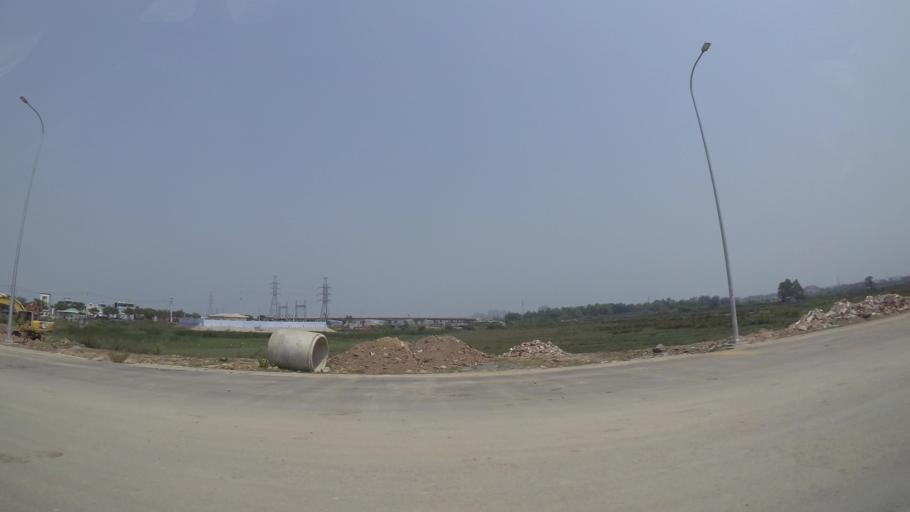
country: VN
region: Da Nang
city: Cam Le
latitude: 15.9991
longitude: 108.2247
